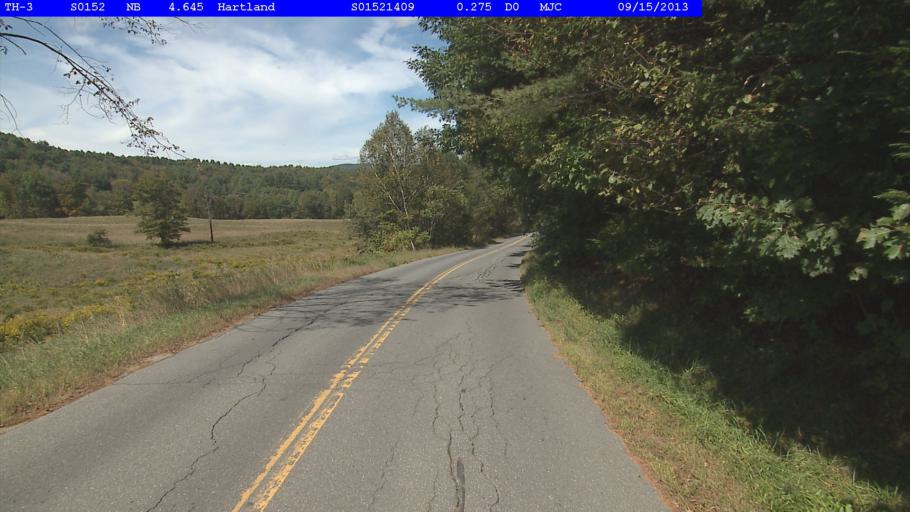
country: US
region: Vermont
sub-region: Windsor County
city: Windsor
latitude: 43.5265
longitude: -72.4366
